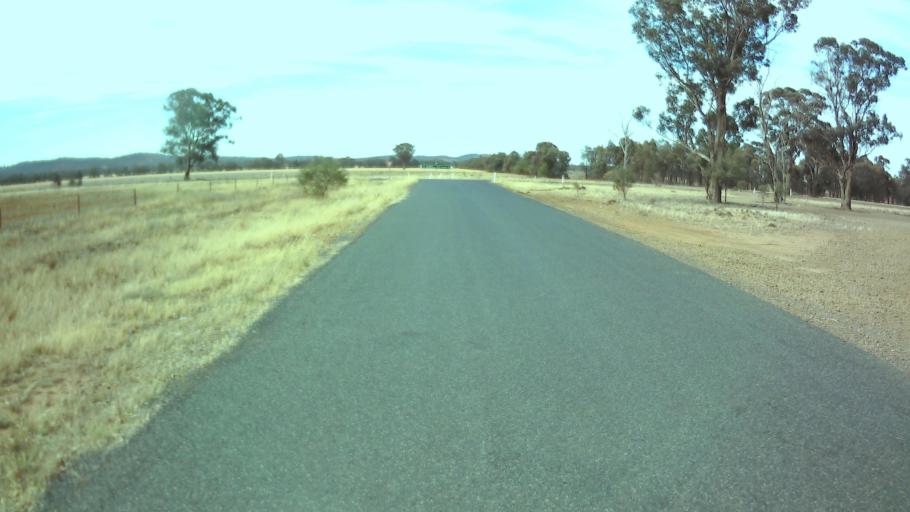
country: AU
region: New South Wales
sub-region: Weddin
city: Grenfell
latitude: -33.8571
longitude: 147.8606
